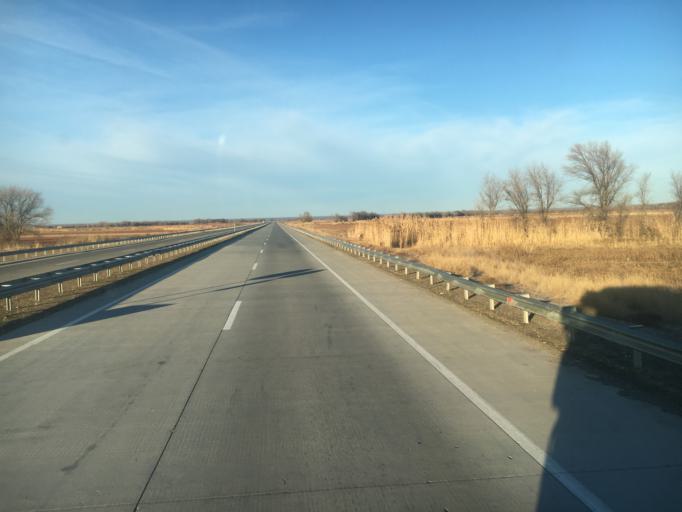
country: KZ
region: Ongtustik Qazaqstan
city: Turkestan
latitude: 43.1563
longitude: 68.5604
